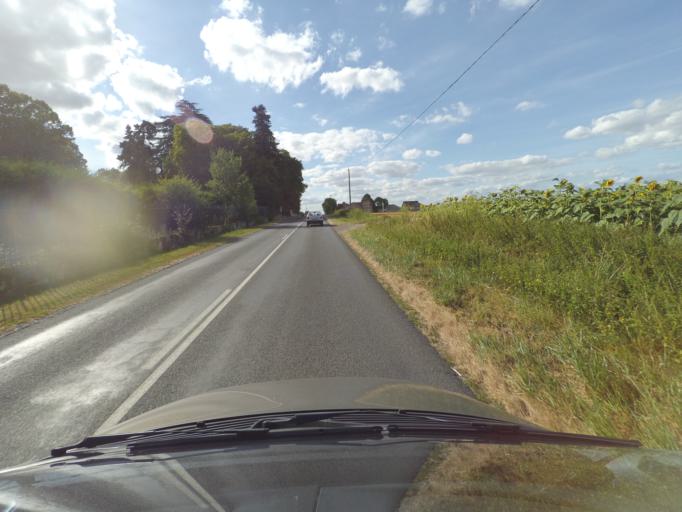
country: FR
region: Poitou-Charentes
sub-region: Departement de la Vienne
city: Saint-Gervais-les-Trois-Clochers
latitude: 46.9580
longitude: 0.3948
